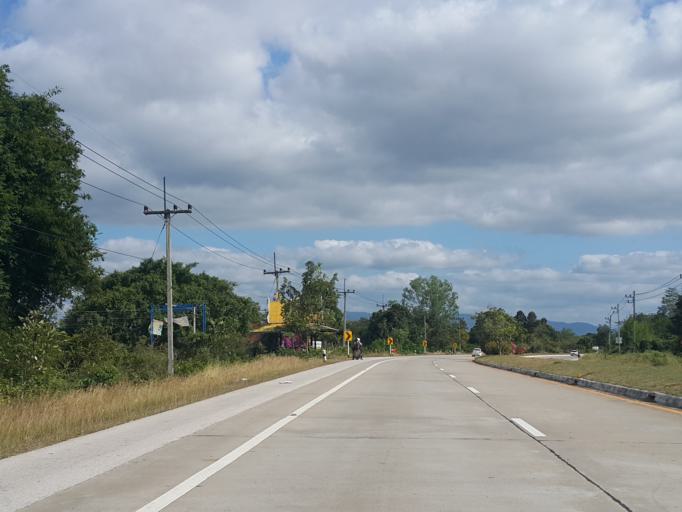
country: TH
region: Lampang
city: Hang Chat
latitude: 18.3251
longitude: 99.4171
